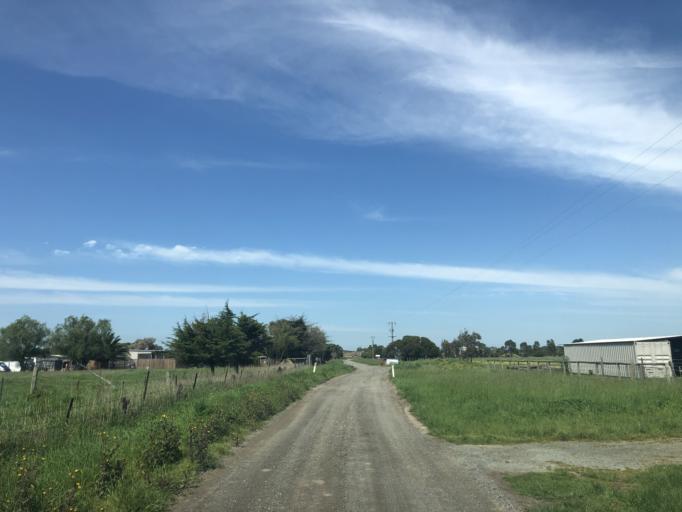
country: AU
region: Victoria
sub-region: Frankston
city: Sandhurst
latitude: -38.0567
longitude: 145.1893
